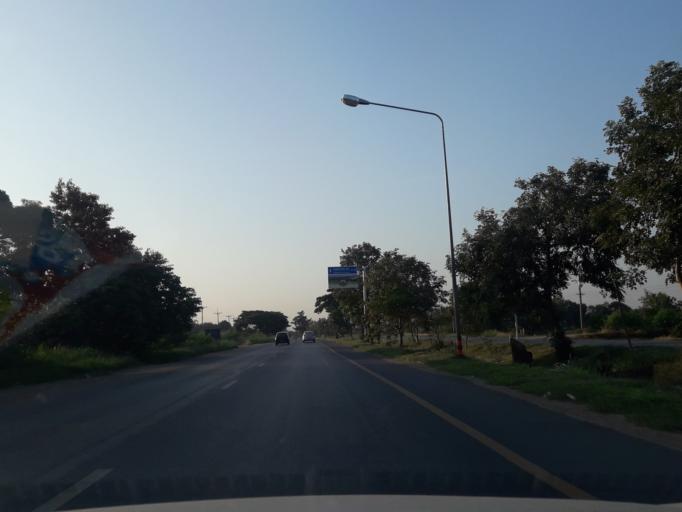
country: TH
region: Phra Nakhon Si Ayutthaya
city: Bang Pa-in
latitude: 14.2259
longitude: 100.5406
